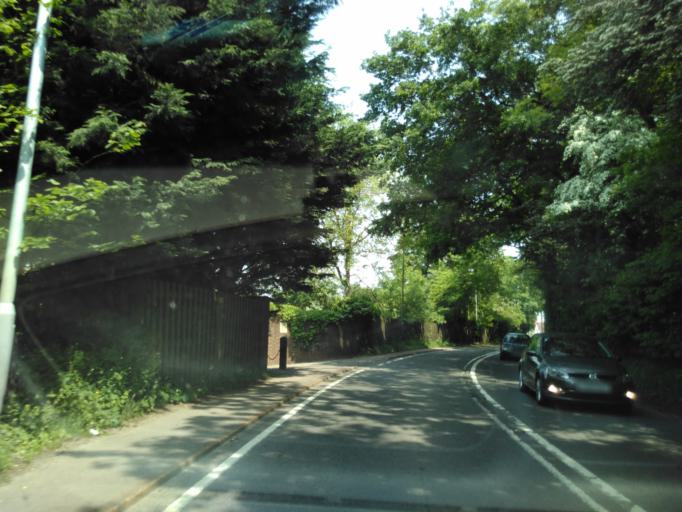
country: GB
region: England
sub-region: Kent
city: Chartham
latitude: 51.2679
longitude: 1.0441
